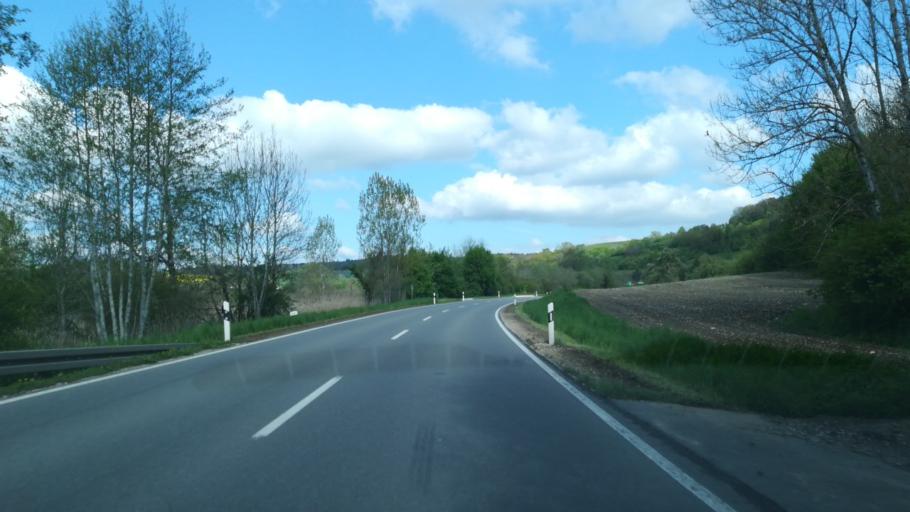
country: CH
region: Schaffhausen
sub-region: Bezirk Reiat
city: Thayngen
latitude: 47.7966
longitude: 8.7093
